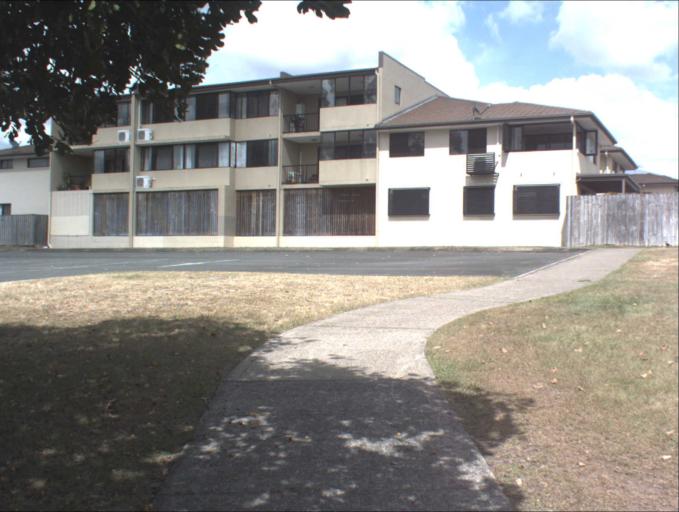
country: AU
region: Queensland
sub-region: Logan
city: Beenleigh
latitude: -27.7173
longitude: 153.1967
